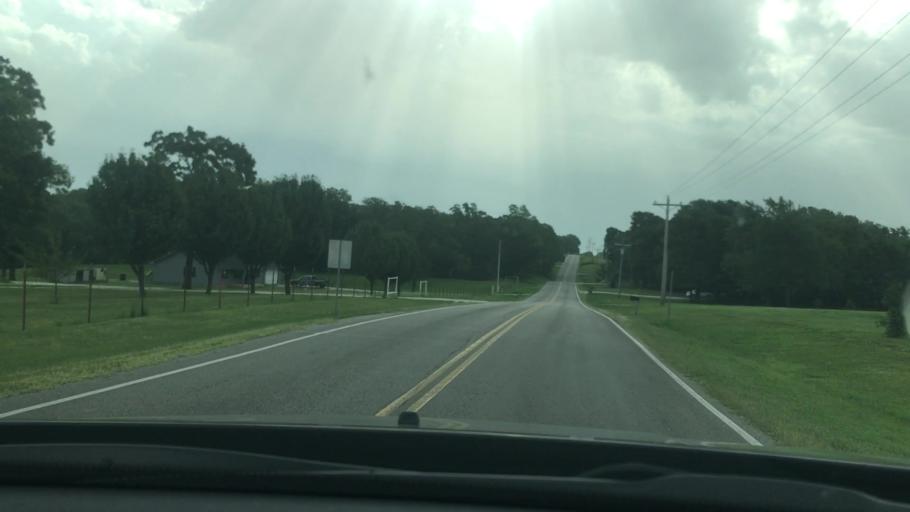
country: US
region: Oklahoma
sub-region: Pontotoc County
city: Ada
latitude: 34.8106
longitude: -96.6346
